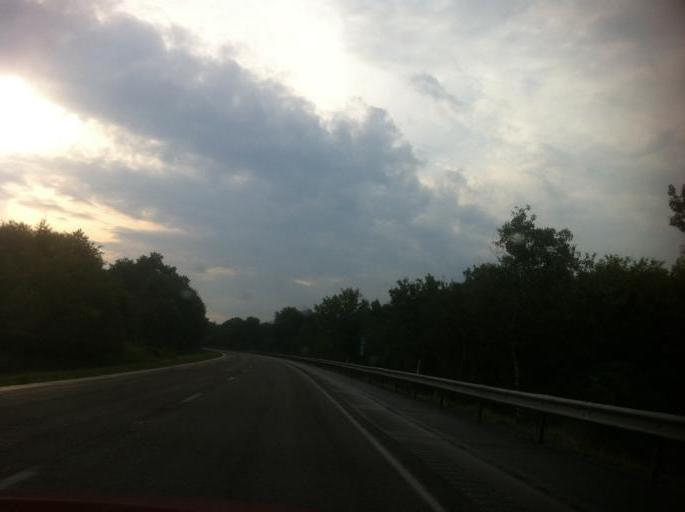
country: US
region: Pennsylvania
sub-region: Clarion County
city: Knox
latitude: 41.1967
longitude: -79.6218
